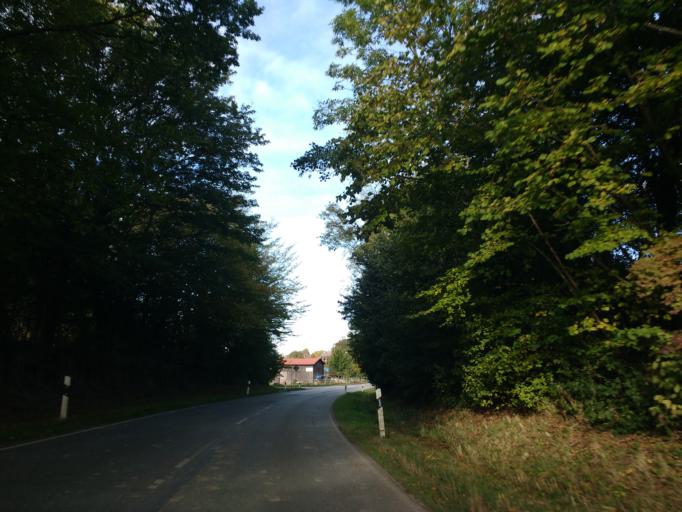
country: DE
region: Schleswig-Holstein
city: Wangels
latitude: 54.2602
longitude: 10.7125
